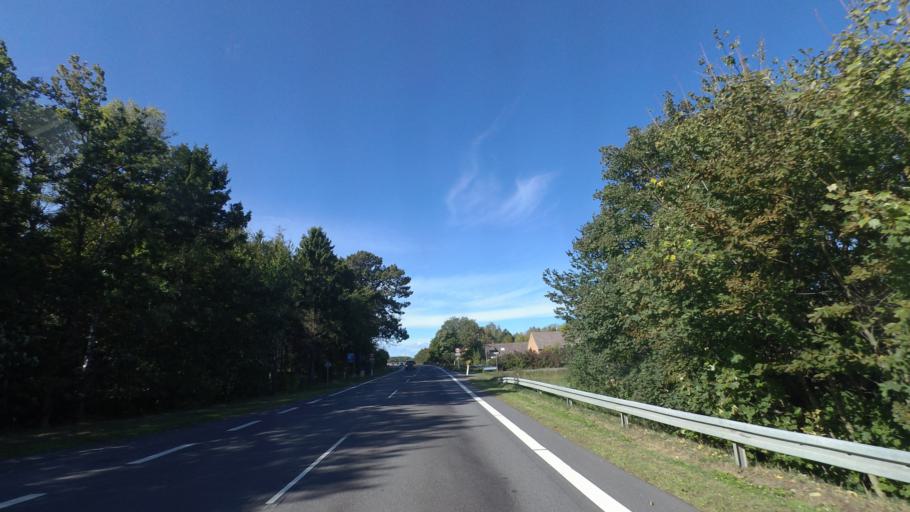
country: DK
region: Capital Region
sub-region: Bornholm Kommune
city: Ronne
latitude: 55.0847
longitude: 14.7485
